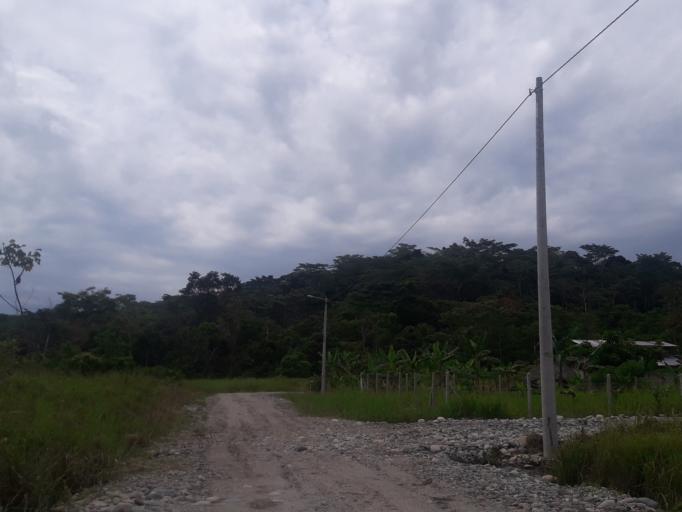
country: EC
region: Napo
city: Tena
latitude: -1.0601
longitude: -77.7949
